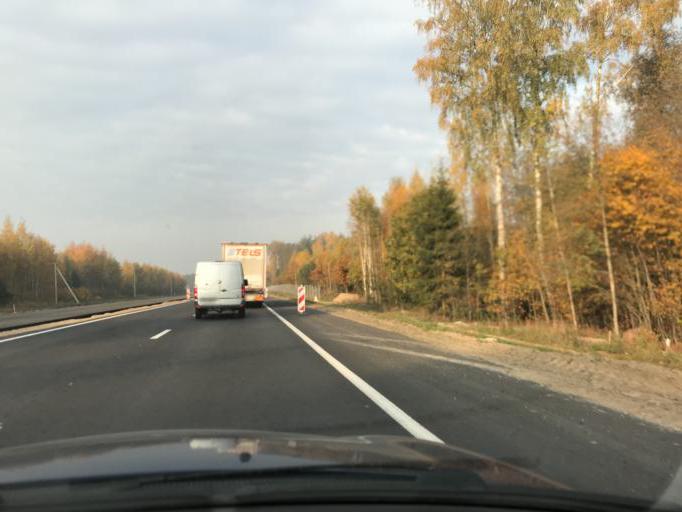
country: BY
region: Grodnenskaya
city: Lida
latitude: 53.8290
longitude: 25.4017
